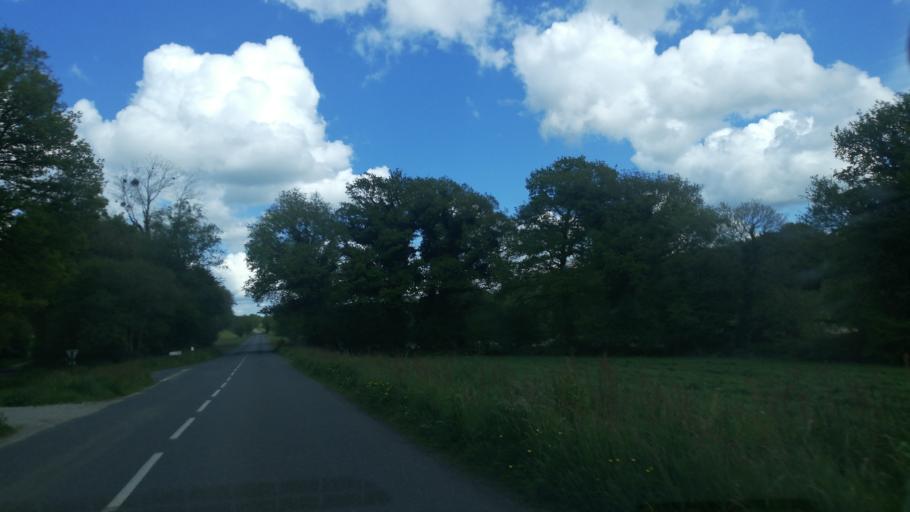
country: FR
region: Brittany
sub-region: Departement des Cotes-d'Armor
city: Saint-Nicolas-du-Pelem
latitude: 48.3165
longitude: -3.1437
